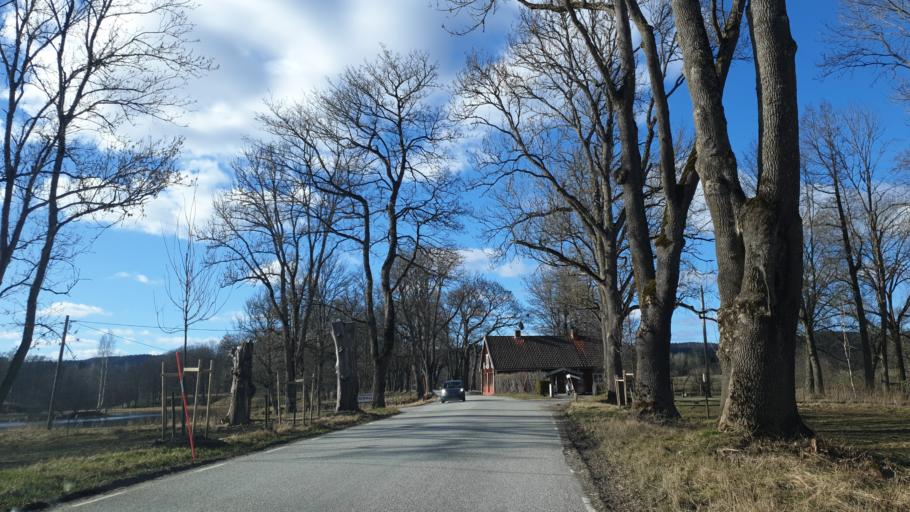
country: SE
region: OErebro
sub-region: Orebro Kommun
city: Garphyttan
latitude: 59.3441
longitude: 15.0097
